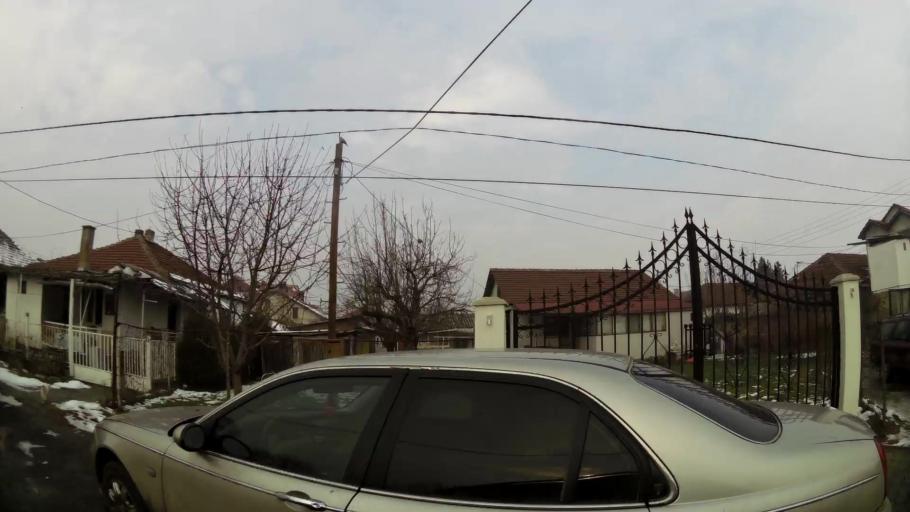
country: MK
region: Ilinden
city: Jurumleri
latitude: 41.9781
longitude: 21.5302
